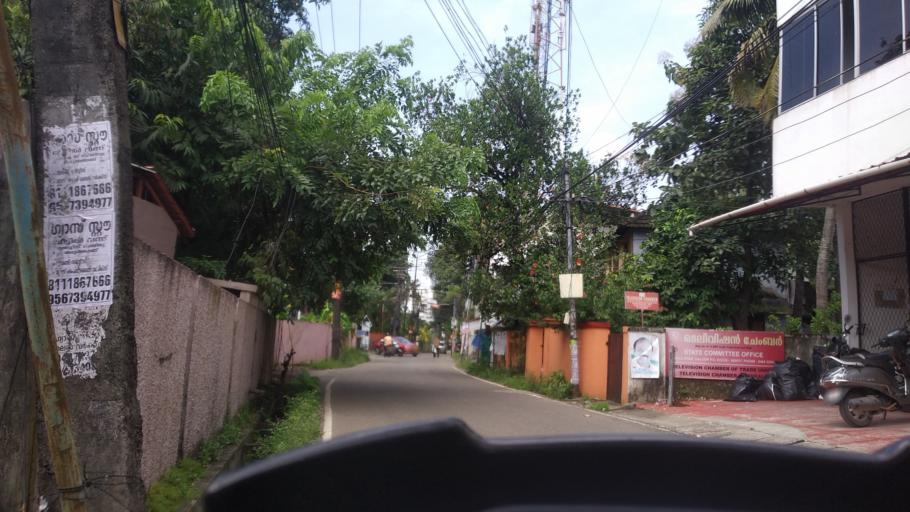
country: IN
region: Kerala
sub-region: Ernakulam
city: Cochin
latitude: 9.9905
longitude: 76.2971
